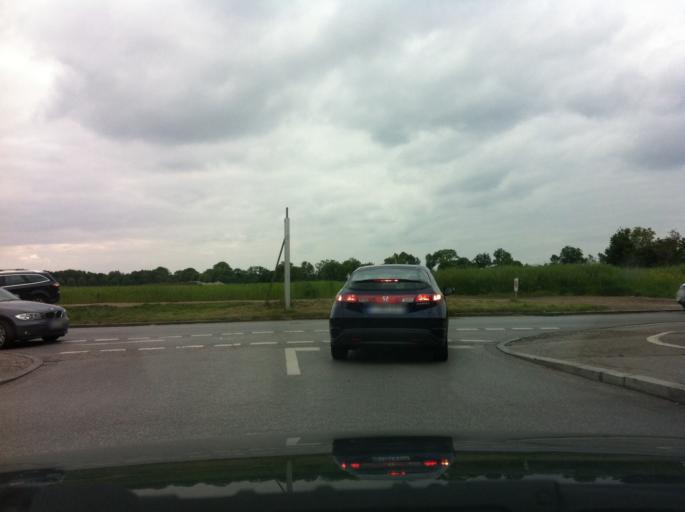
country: DE
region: Bavaria
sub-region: Upper Bavaria
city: Unterhaching
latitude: 48.0924
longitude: 11.6251
